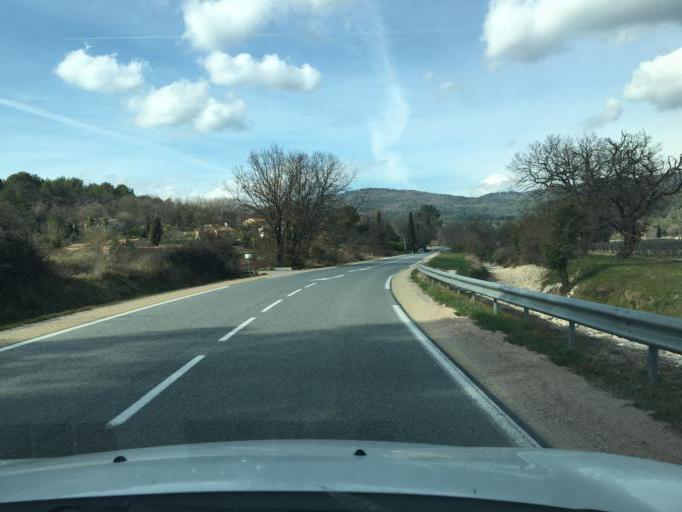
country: FR
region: Provence-Alpes-Cote d'Azur
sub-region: Departement du Var
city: Figanieres
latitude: 43.5588
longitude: 6.5135
